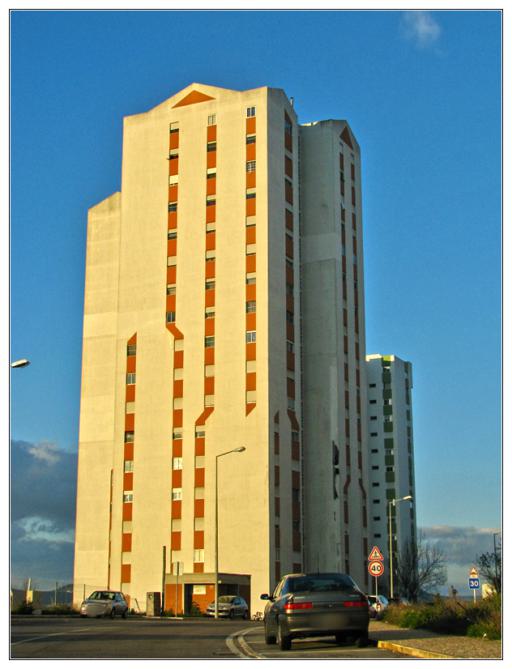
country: PT
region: Lisbon
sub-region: Odivelas
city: Povoa de Santo Adriao
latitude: 38.8113
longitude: -9.1691
